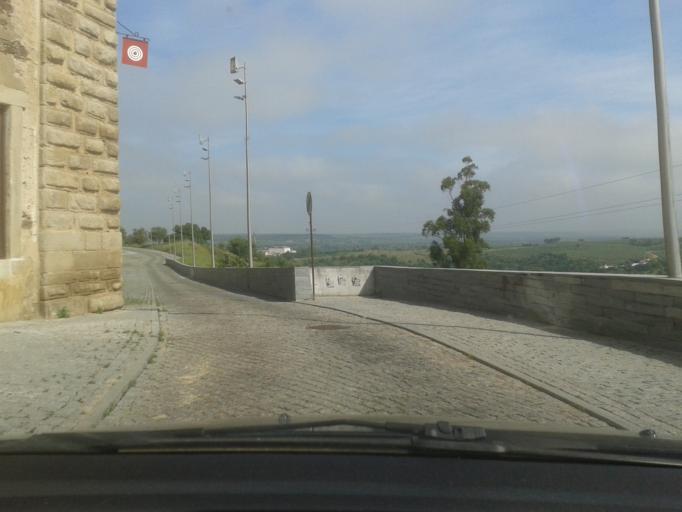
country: PT
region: Portalegre
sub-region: Avis
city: Avis
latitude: 39.0564
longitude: -7.8884
